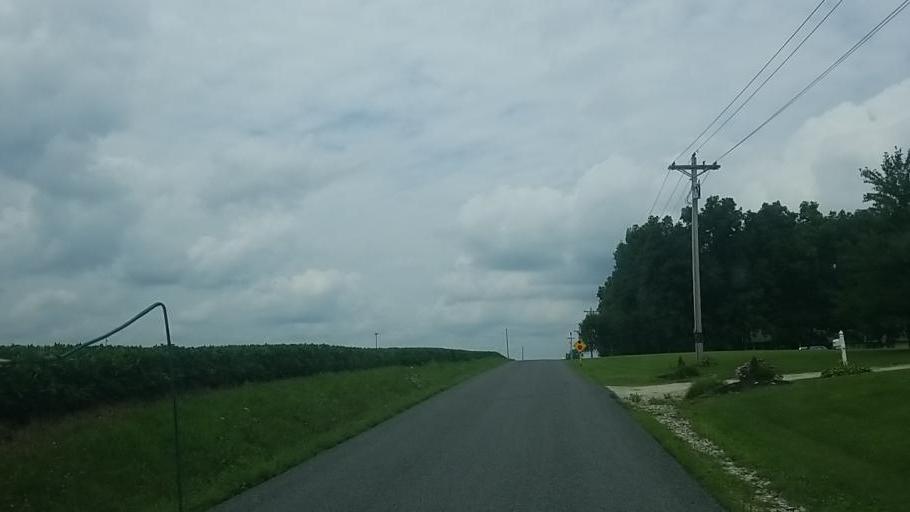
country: US
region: Ohio
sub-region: Licking County
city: Utica
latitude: 40.2399
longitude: -82.3914
